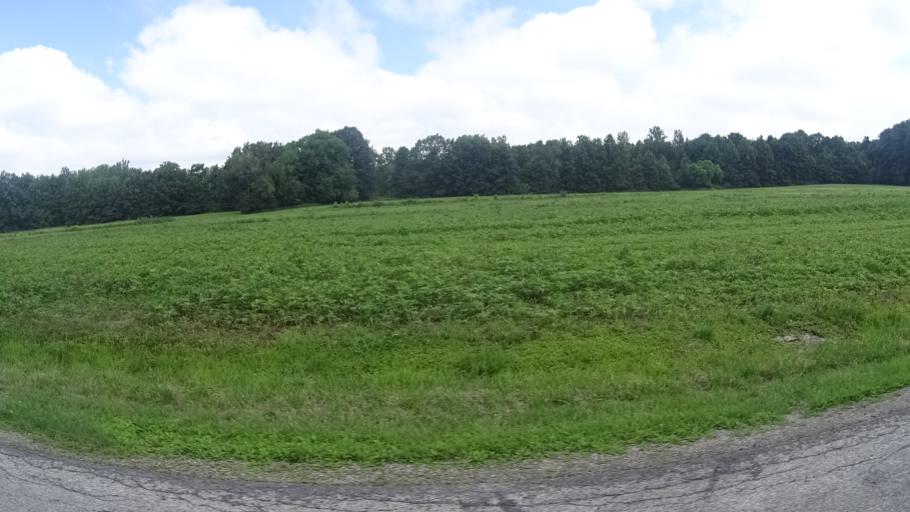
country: US
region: Ohio
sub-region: Huron County
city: Wakeman
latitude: 41.3151
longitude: -82.3907
